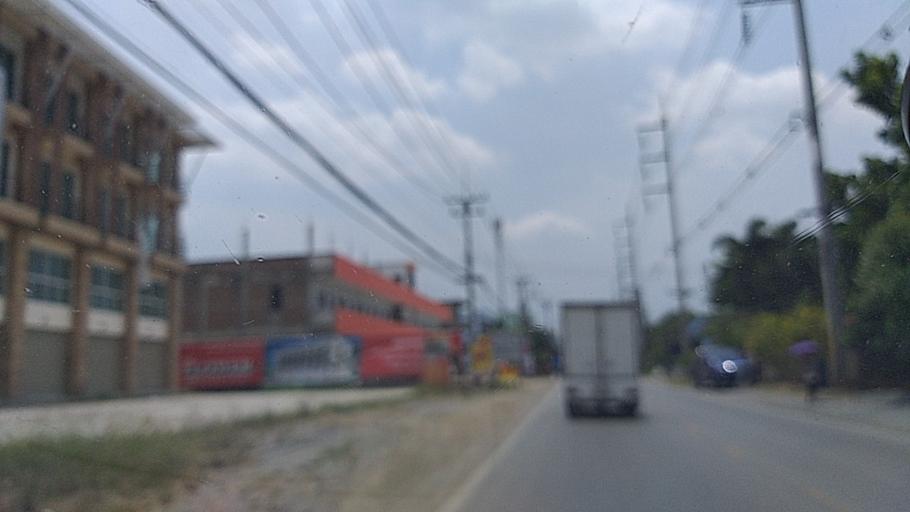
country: TH
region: Nakhon Pathom
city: Salaya
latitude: 13.7613
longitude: 100.2849
